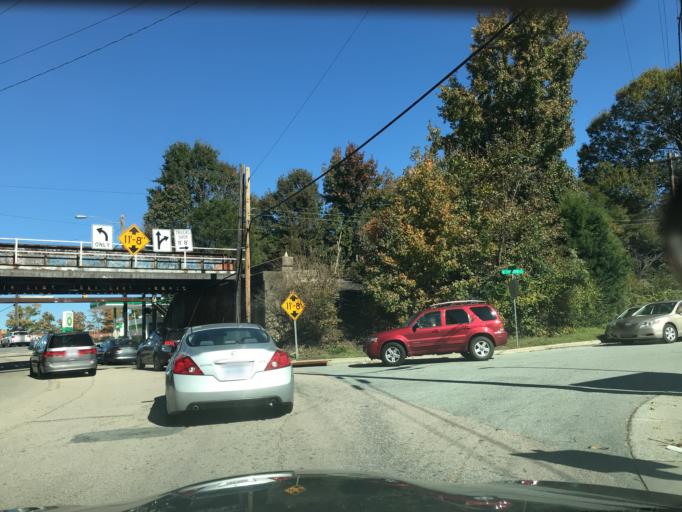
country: US
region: North Carolina
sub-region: Durham County
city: Durham
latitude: 36.0060
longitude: -78.9224
